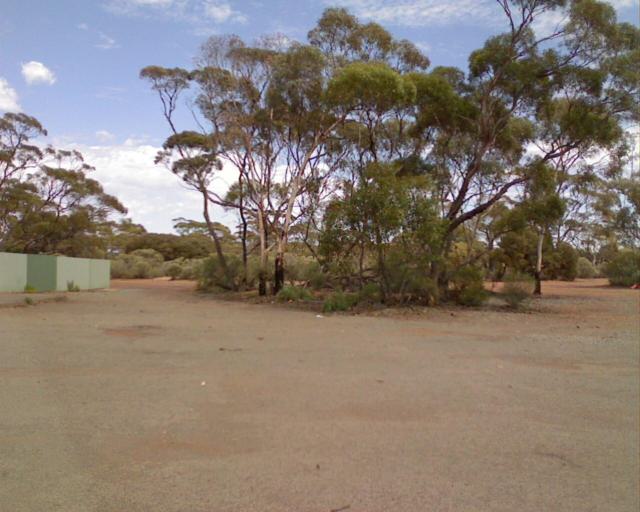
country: AU
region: Western Australia
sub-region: Kalgoorlie/Boulder
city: Stoneville
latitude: -31.2146
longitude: 121.6267
